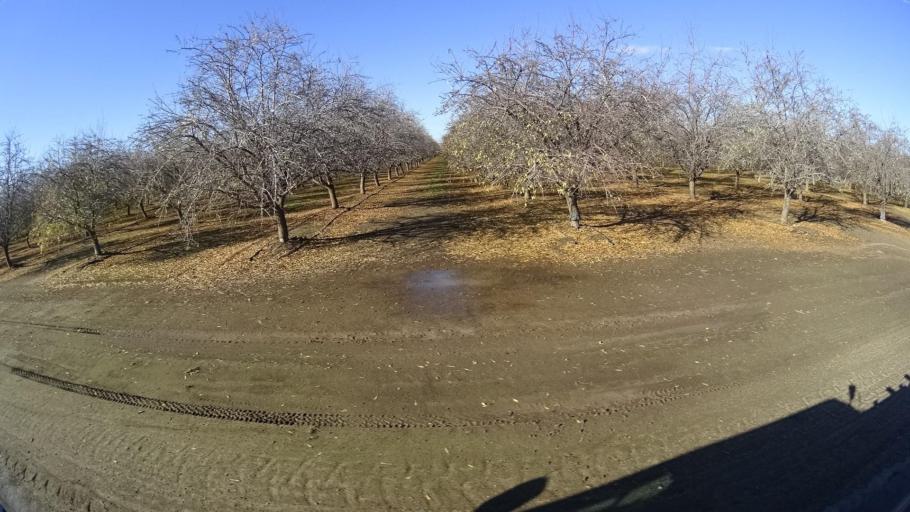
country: US
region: California
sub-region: Kern County
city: McFarland
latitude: 35.6919
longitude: -119.2764
